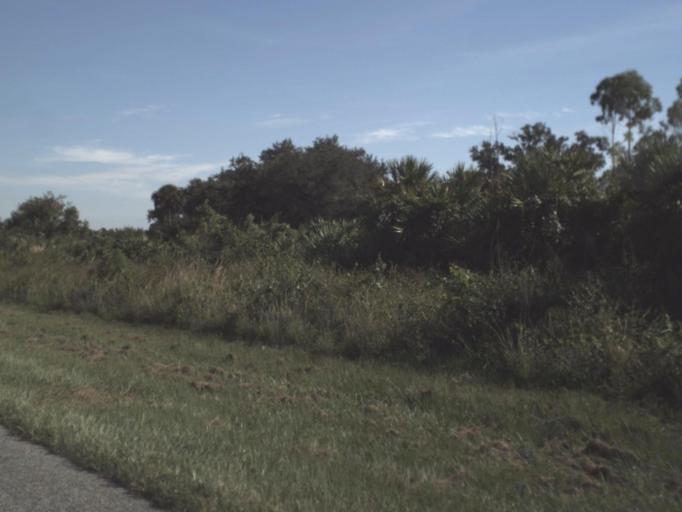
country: US
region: Florida
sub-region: Hendry County
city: Port LaBelle
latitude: 26.9135
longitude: -81.2823
